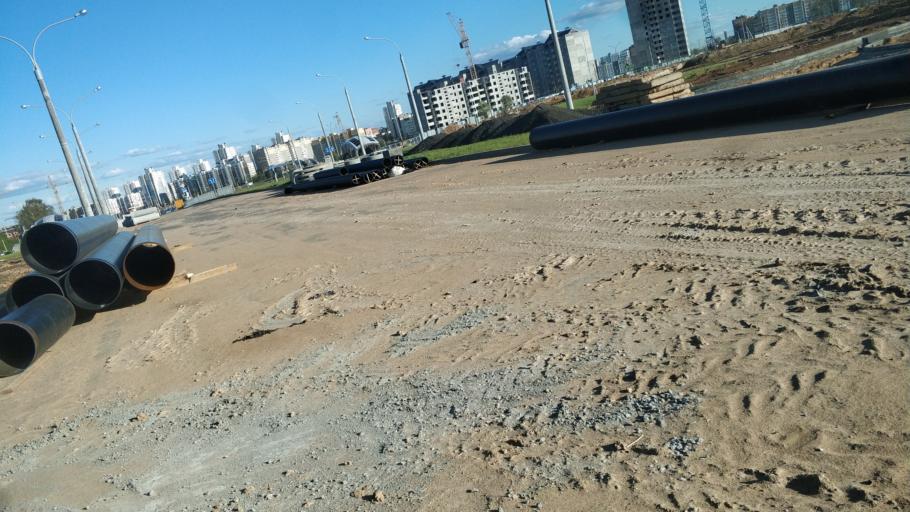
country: BY
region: Minsk
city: Syenitsa
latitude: 53.8461
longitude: 27.5731
